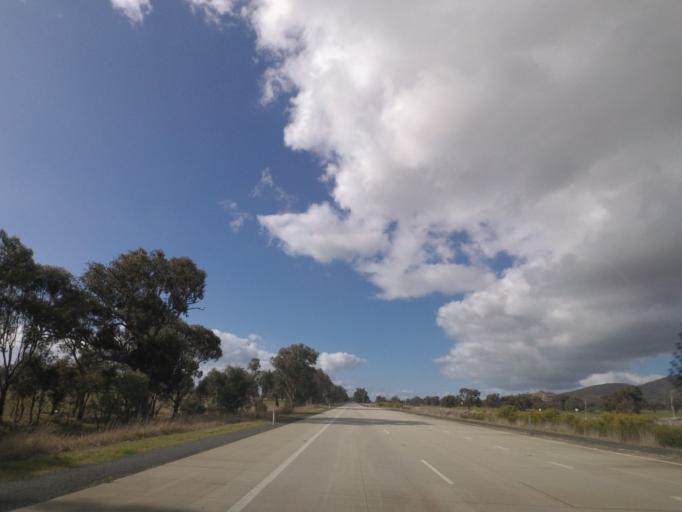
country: AU
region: New South Wales
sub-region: Greater Hume Shire
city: Holbrook
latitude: -35.6934
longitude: 147.3441
